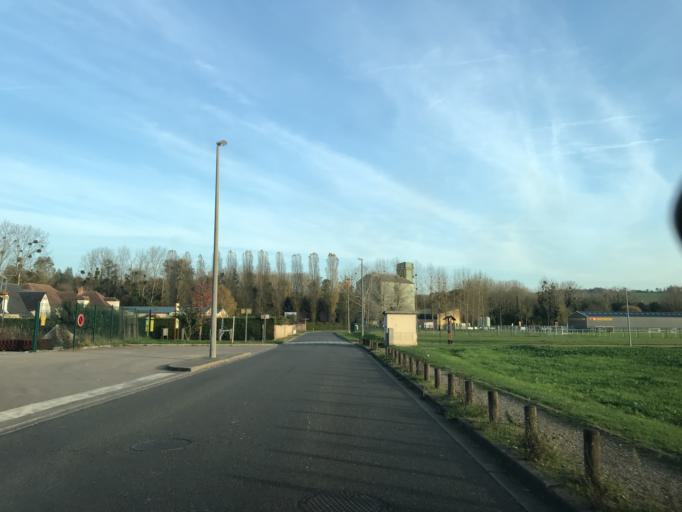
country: FR
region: Haute-Normandie
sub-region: Departement de l'Eure
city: Gasny
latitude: 49.0955
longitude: 1.6097
